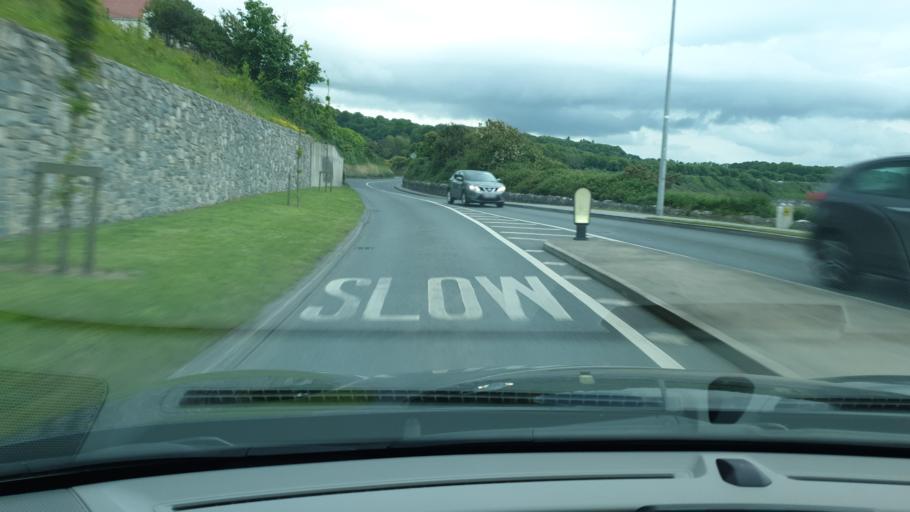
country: IE
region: Leinster
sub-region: Fingal County
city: Skerries
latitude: 53.5855
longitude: -6.1442
